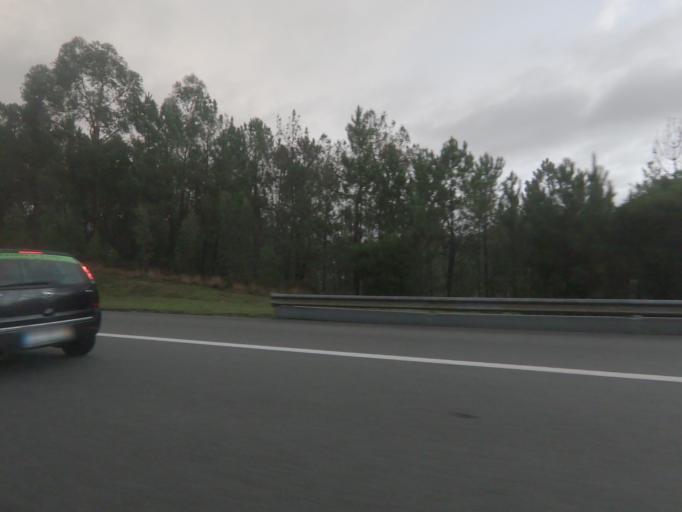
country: PT
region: Viana do Castelo
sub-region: Ponte de Lima
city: Ponte de Lima
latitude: 41.7564
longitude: -8.5583
